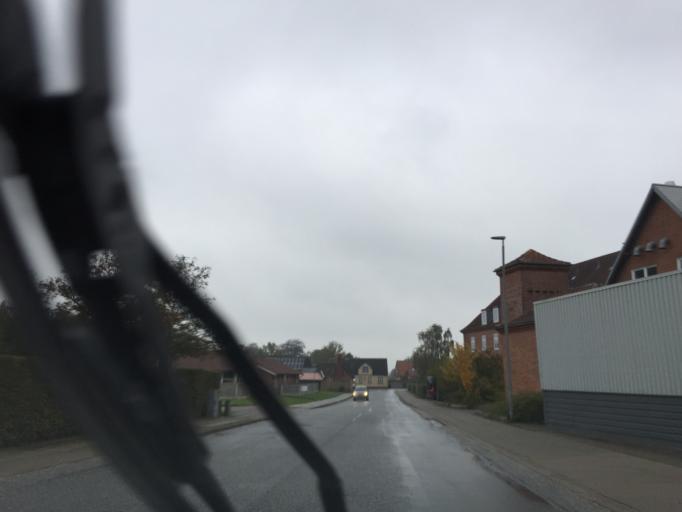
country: DK
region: Central Jutland
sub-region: Silkeborg Kommune
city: Kjellerup
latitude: 56.2864
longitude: 9.4231
